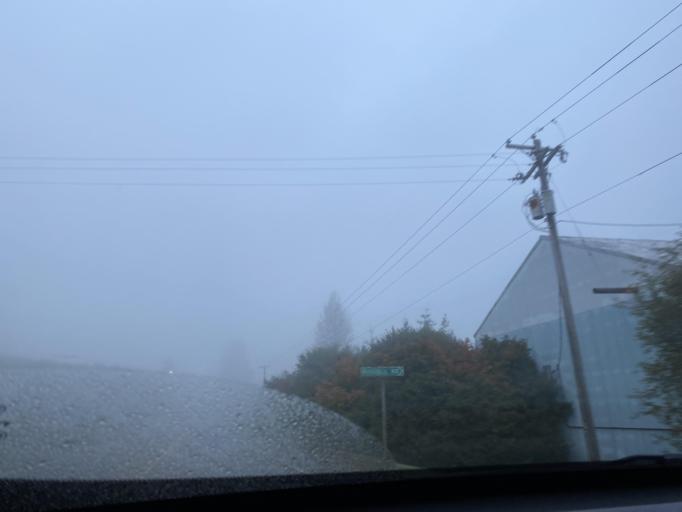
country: US
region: Washington
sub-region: Clallam County
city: Forks
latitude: 47.9353
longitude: -124.3997
